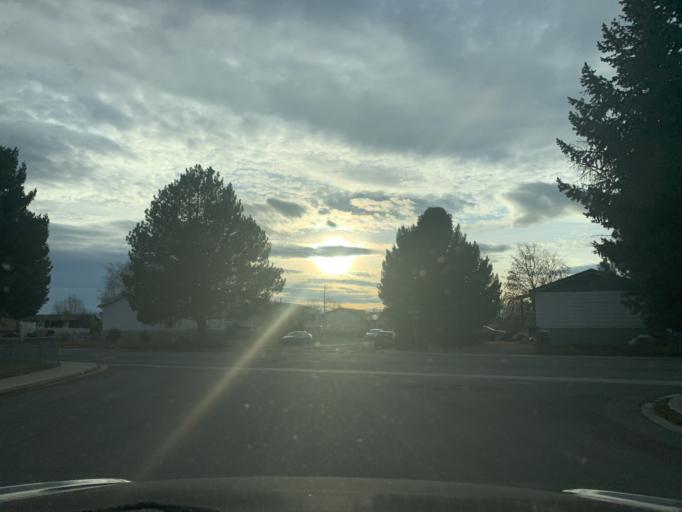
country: US
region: Utah
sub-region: Utah County
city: Provo
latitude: 40.2183
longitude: -111.6703
